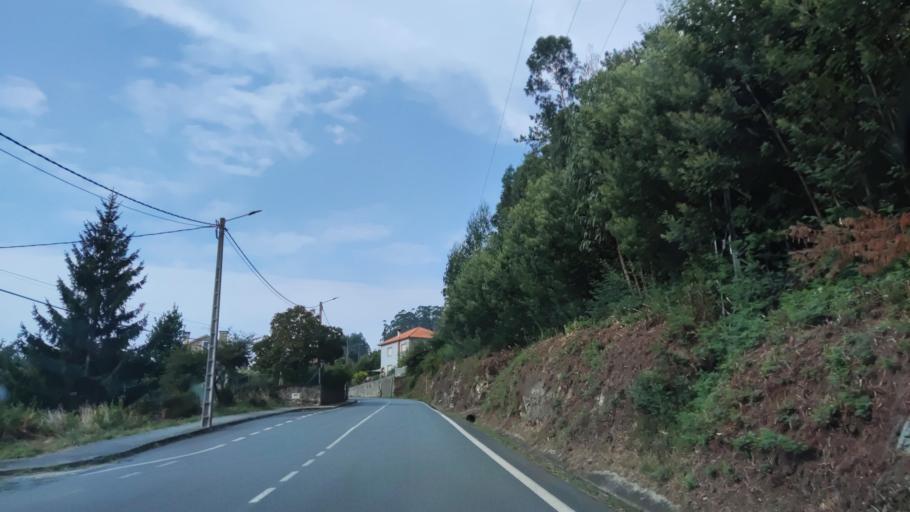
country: ES
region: Galicia
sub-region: Provincia da Coruna
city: Rianxo
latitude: 42.6536
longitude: -8.7763
